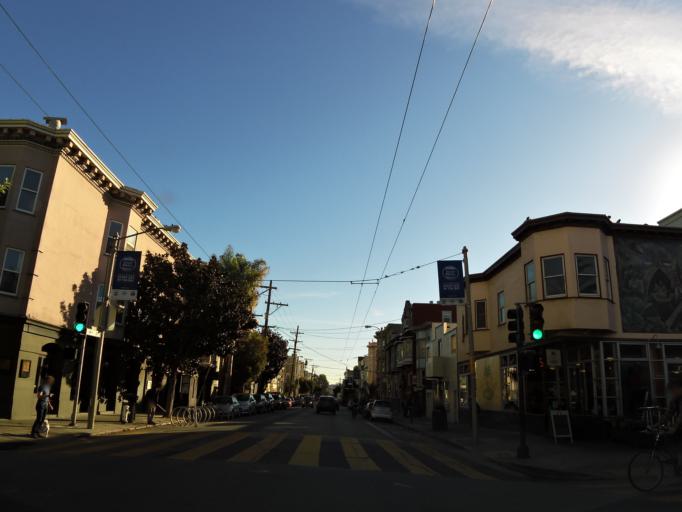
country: US
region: California
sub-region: San Francisco County
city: San Francisco
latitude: 37.7614
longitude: -122.4260
